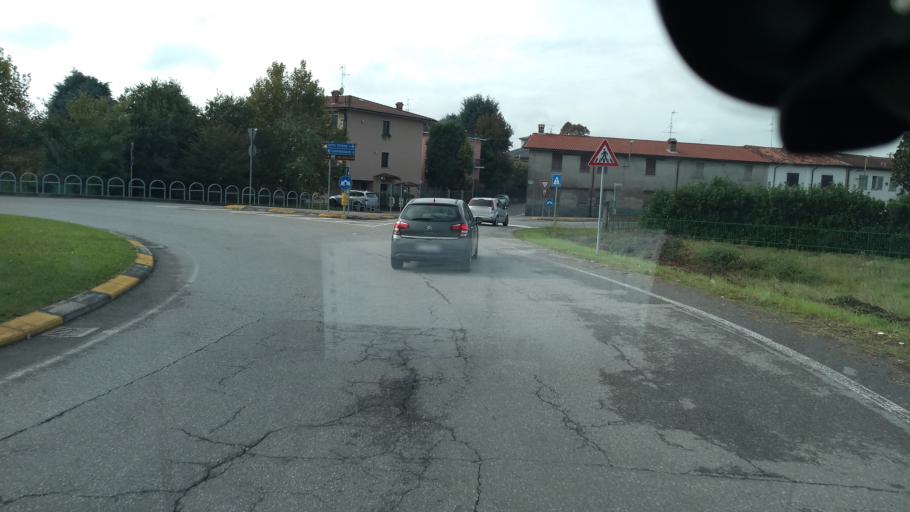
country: IT
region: Lombardy
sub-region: Provincia di Bergamo
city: Brignano Gera d'Adda
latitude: 45.5470
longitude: 9.6429
